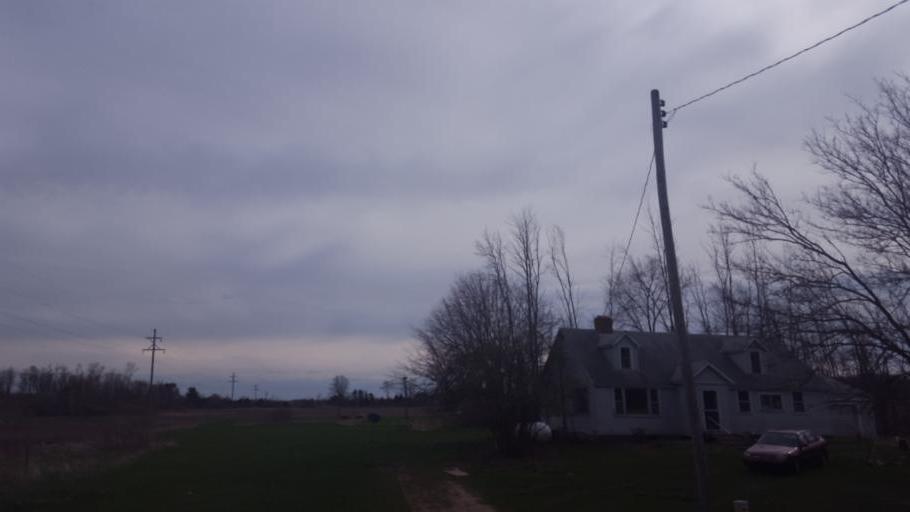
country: US
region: Michigan
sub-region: Clare County
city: Clare
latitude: 43.8728
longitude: -84.7495
